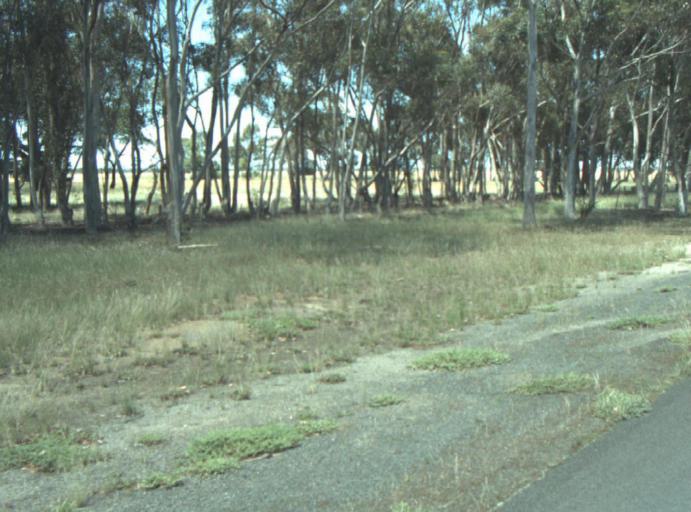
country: AU
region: Victoria
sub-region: Greater Geelong
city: Lara
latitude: -37.9401
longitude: 144.3578
